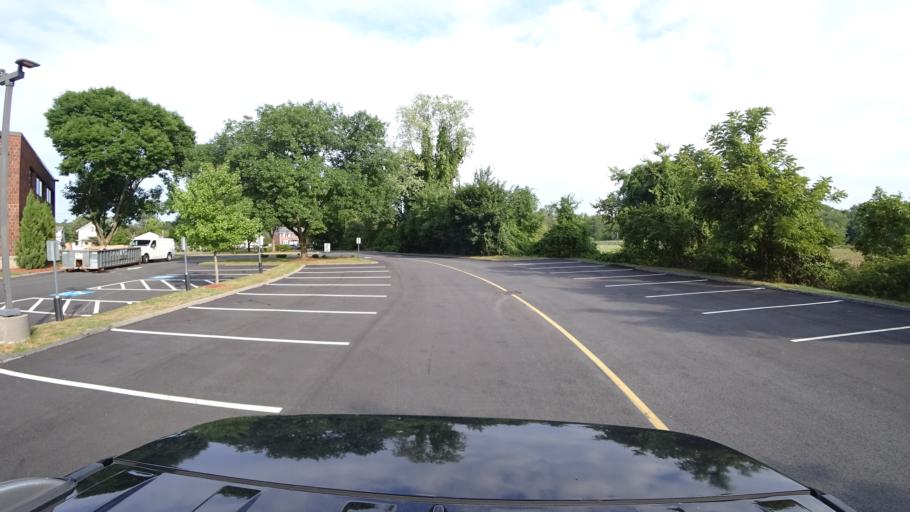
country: US
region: Massachusetts
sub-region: Norfolk County
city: Dedham
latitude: 42.2623
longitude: -71.1762
